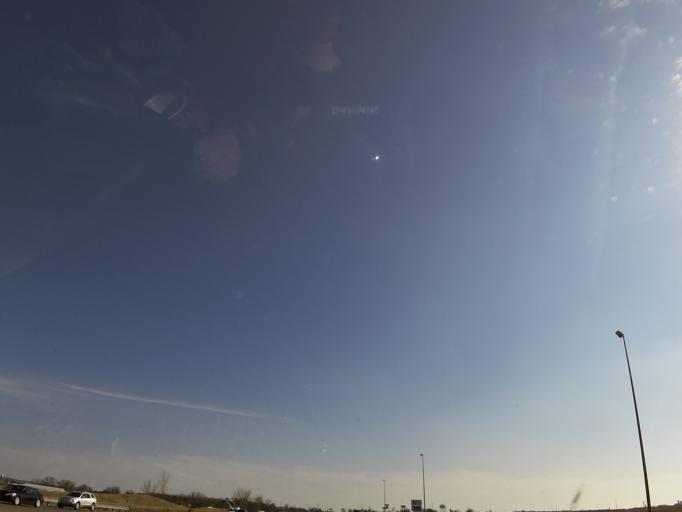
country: US
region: Minnesota
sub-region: Steele County
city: Owatonna
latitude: 44.1057
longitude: -93.2459
